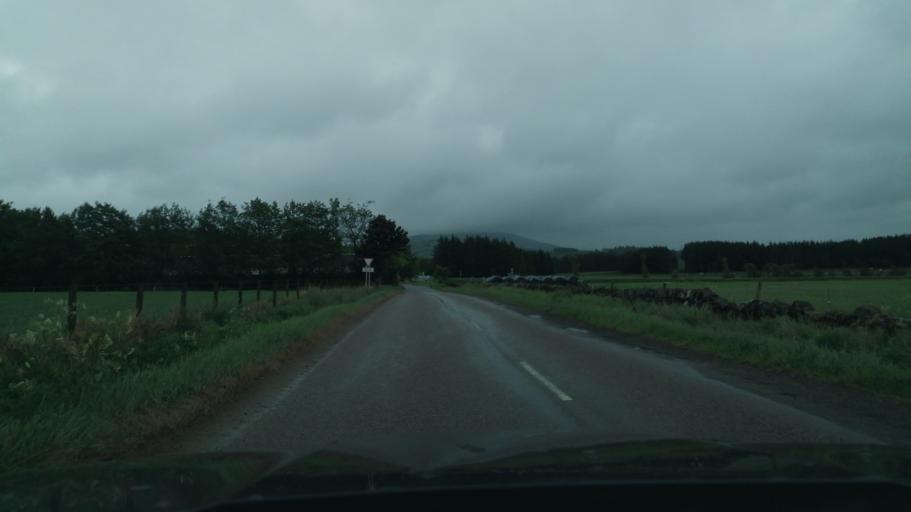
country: GB
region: Scotland
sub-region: Aberdeenshire
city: Huntly
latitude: 57.5351
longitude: -2.7705
